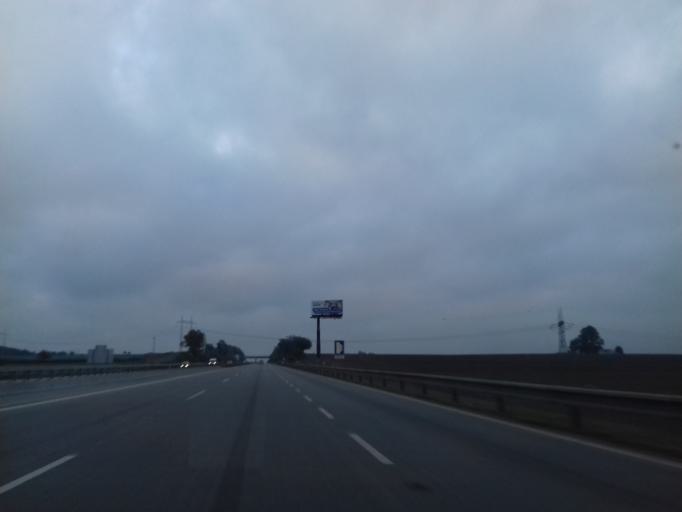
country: CZ
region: Central Bohemia
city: Cechtice
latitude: 49.6550
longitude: 15.1222
